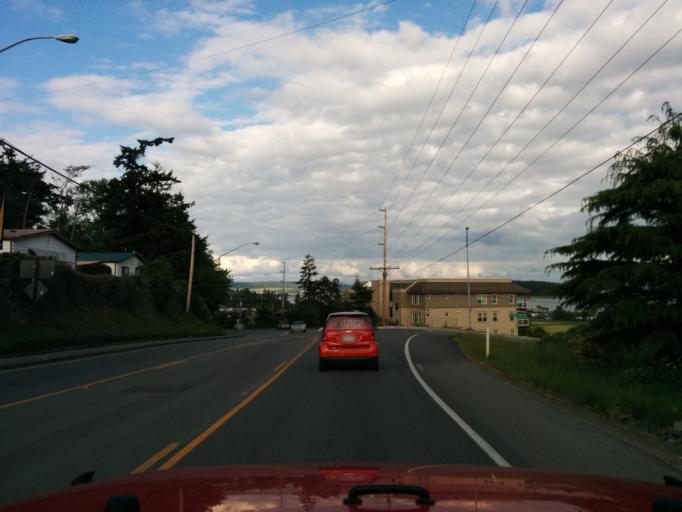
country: US
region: Washington
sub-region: Island County
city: Oak Harbor
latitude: 48.2841
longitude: -122.6672
